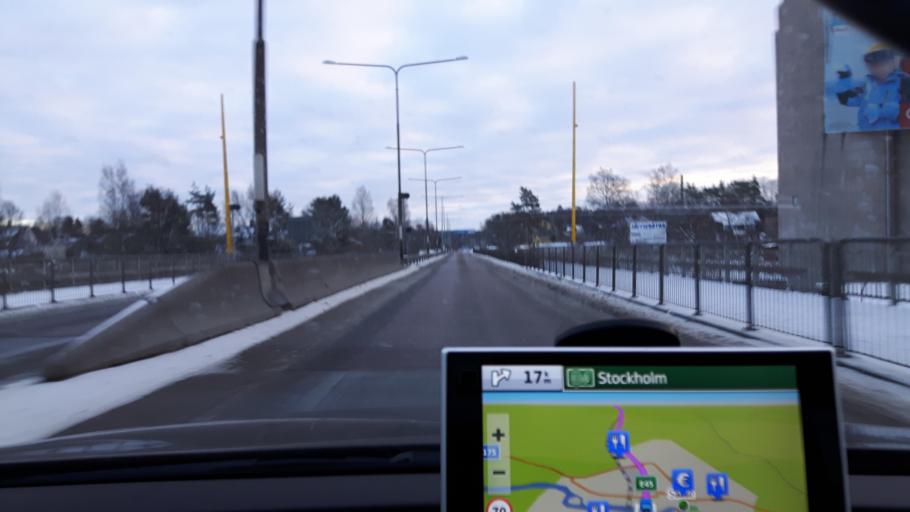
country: SE
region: Vaermland
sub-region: Saffle Kommun
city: Saeffle
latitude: 59.1362
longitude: 12.9235
